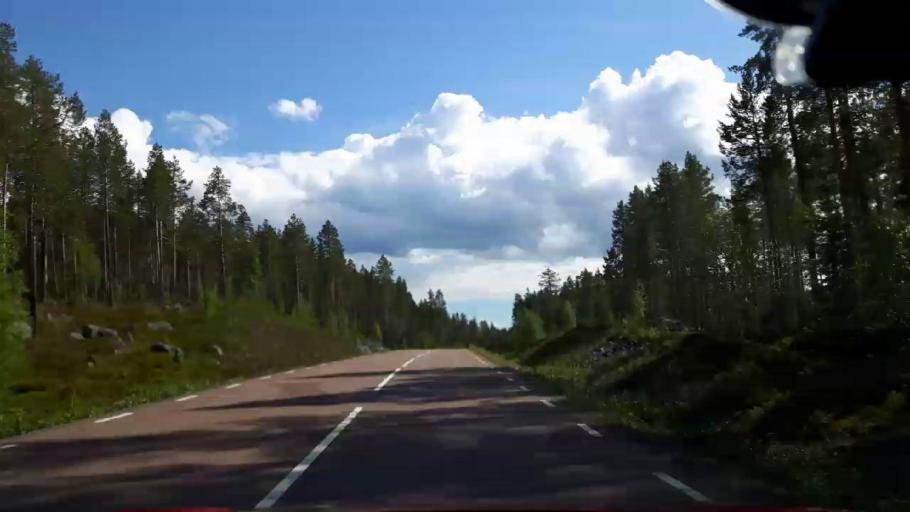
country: SE
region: Jaemtland
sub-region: Krokoms Kommun
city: Valla
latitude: 64.0042
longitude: 14.2400
